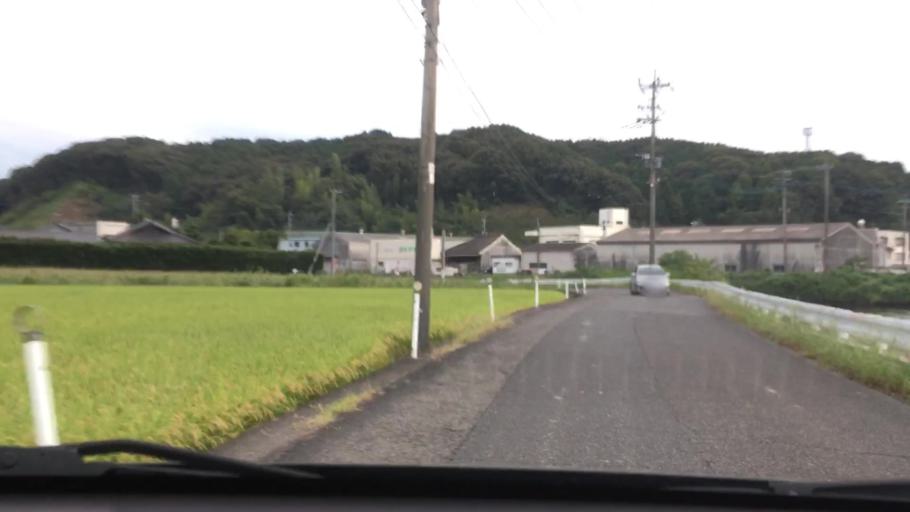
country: JP
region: Nagasaki
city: Togitsu
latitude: 32.9893
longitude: 129.7734
